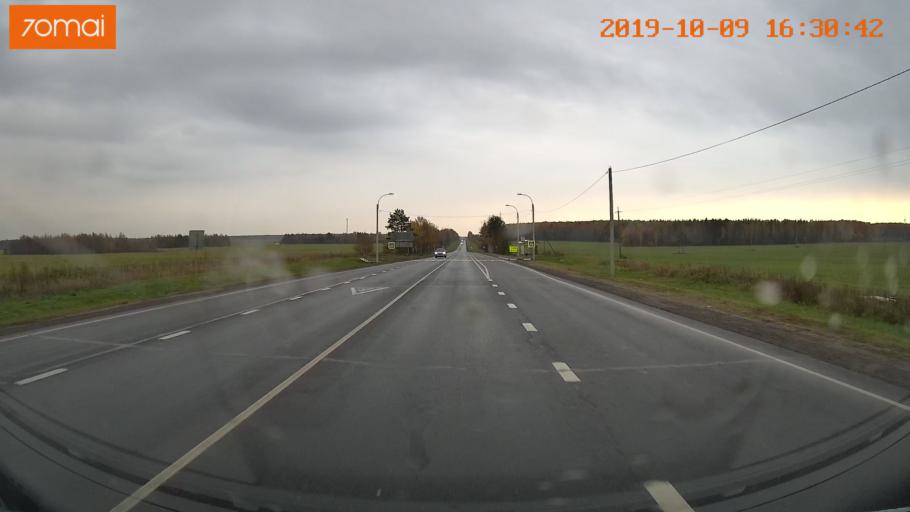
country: RU
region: Kostroma
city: Oktyabr'skiy
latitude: 57.6160
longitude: 40.9431
